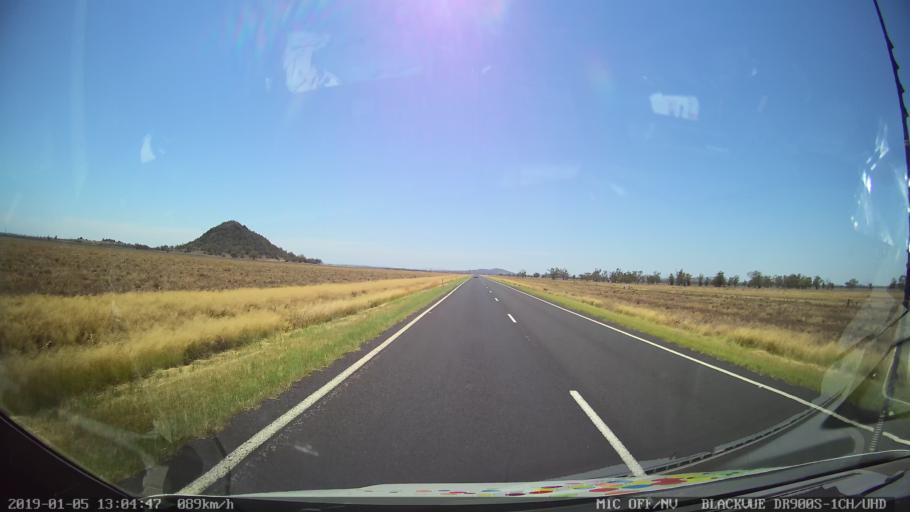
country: AU
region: New South Wales
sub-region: Gunnedah
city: Gunnedah
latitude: -31.1004
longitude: 149.8446
